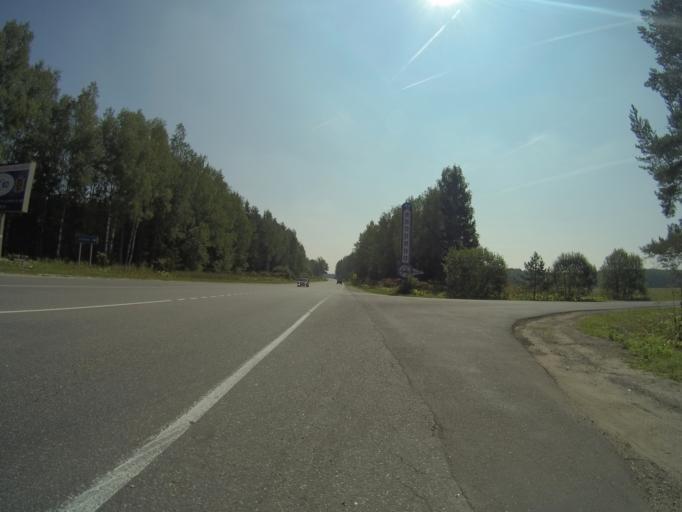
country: RU
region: Vladimir
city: Anopino
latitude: 55.7395
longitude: 40.7100
